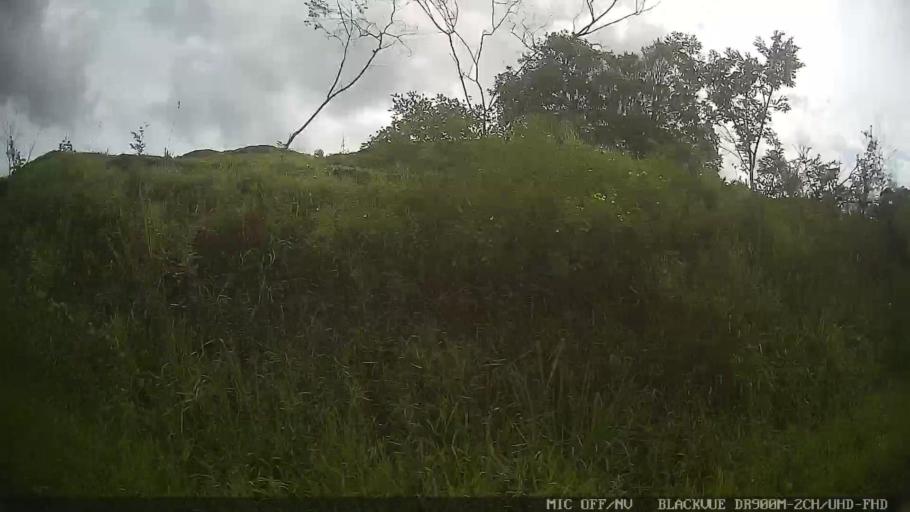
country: BR
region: Minas Gerais
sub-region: Extrema
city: Extrema
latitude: -22.7655
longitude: -46.3581
